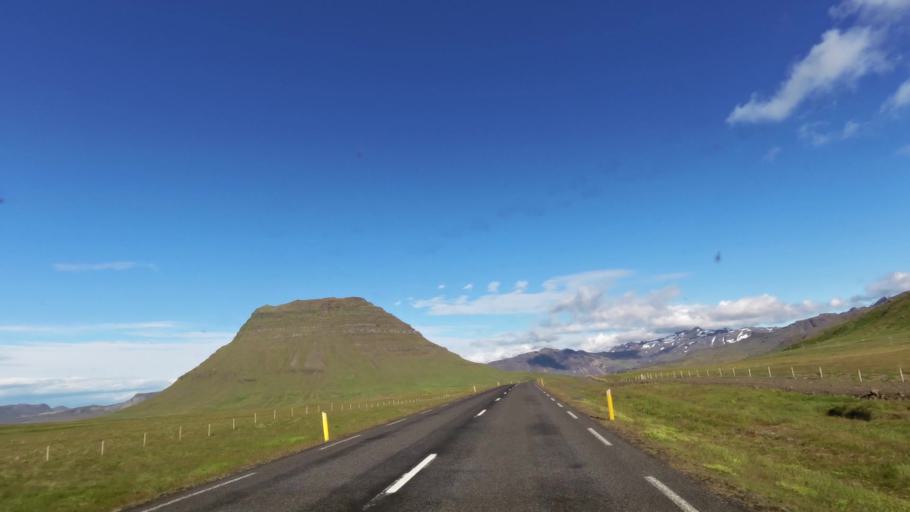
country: IS
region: West
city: Olafsvik
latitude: 64.9401
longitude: -23.3667
